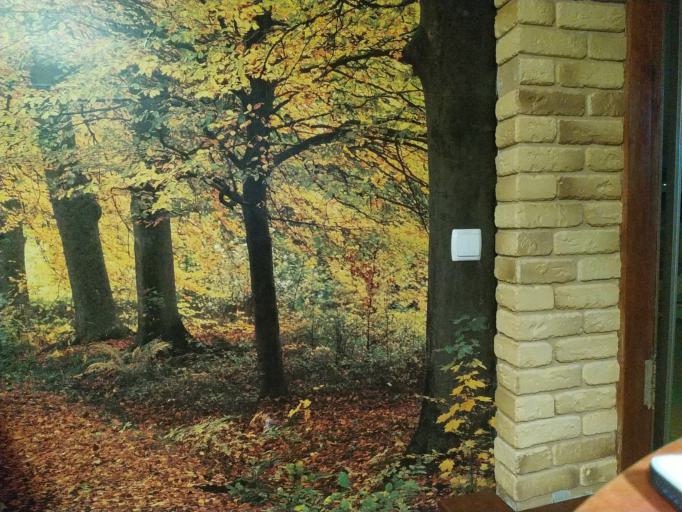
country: RU
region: Novgorod
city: Okulovka
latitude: 58.5451
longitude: 33.2681
